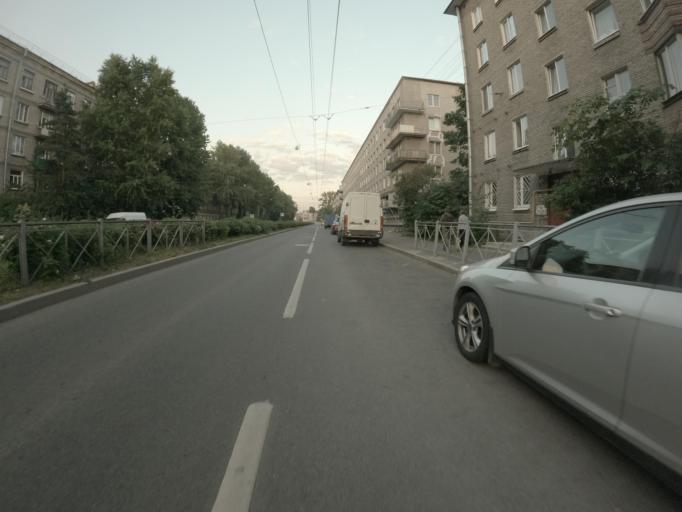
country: RU
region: St.-Petersburg
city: Avtovo
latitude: 59.8773
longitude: 30.2731
